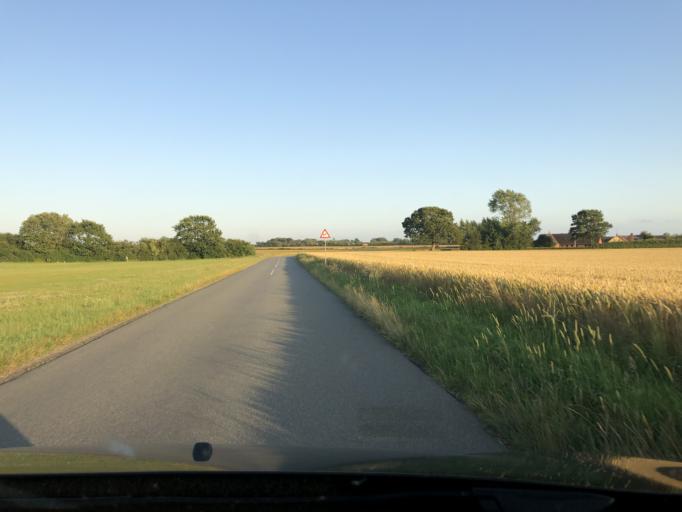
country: DK
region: South Denmark
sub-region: Vejle Kommune
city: Brejning
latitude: 55.6492
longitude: 9.6864
